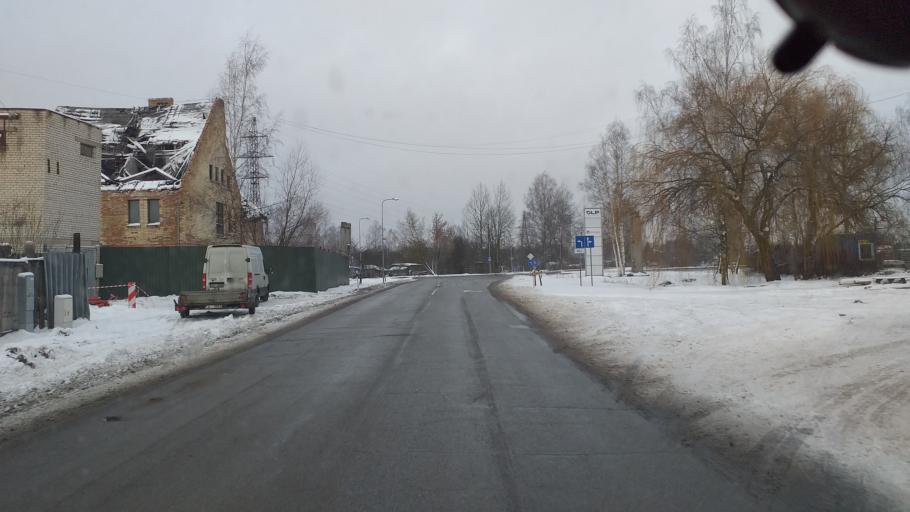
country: LV
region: Olaine
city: Olaine
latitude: 56.7954
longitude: 23.9387
